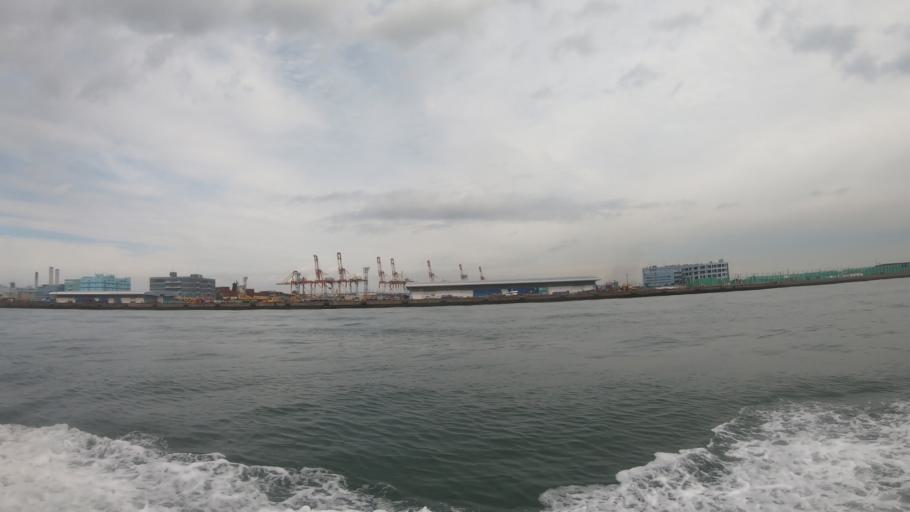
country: JP
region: Kanagawa
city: Yokohama
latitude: 35.4508
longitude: 139.6890
